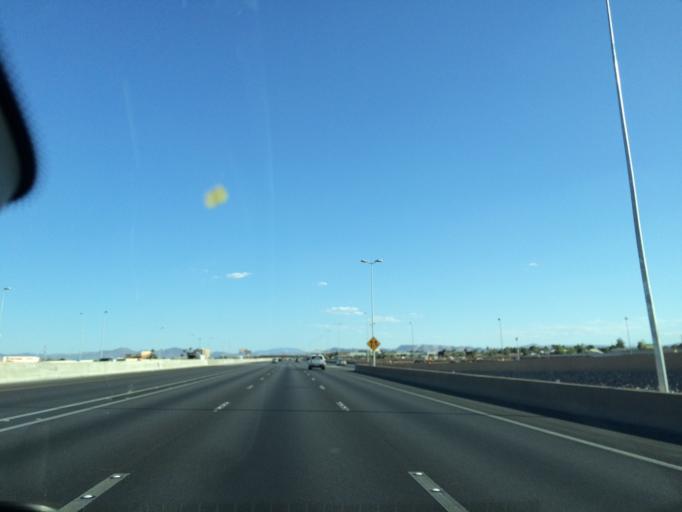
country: US
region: Nevada
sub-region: Clark County
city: Paradise
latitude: 36.0672
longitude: -115.1809
